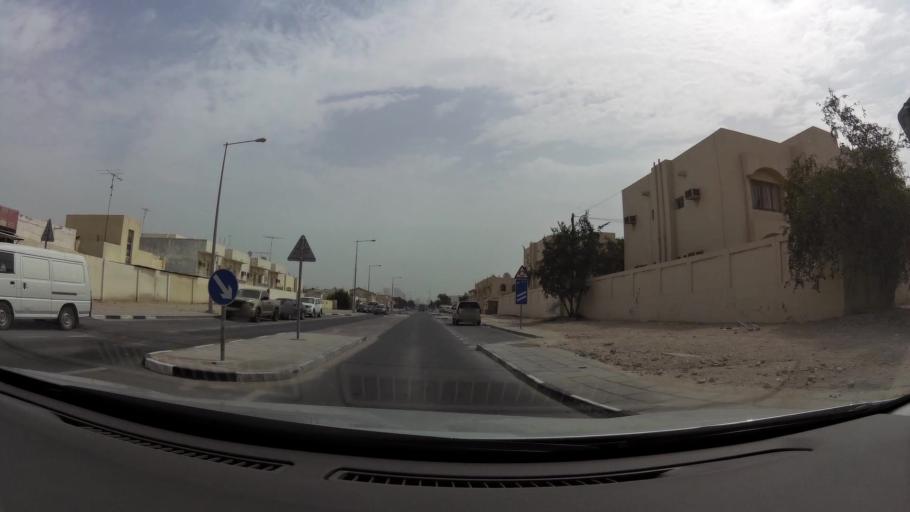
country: QA
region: Baladiyat ad Dawhah
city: Doha
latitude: 25.3106
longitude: 51.4767
